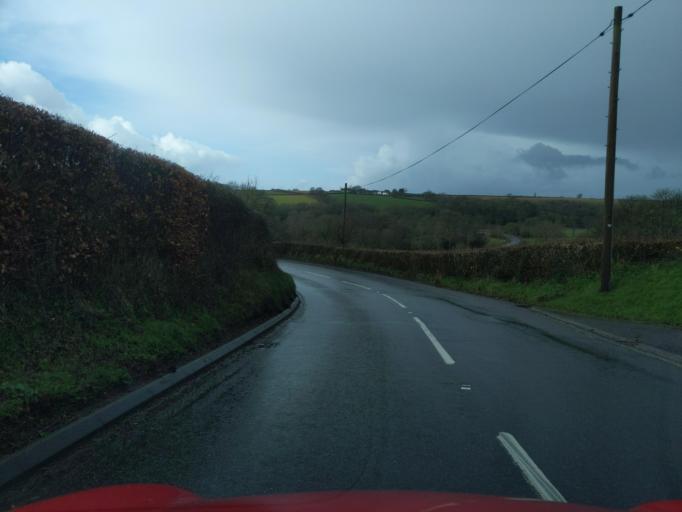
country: GB
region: England
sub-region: Devon
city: Okehampton
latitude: 50.8338
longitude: -4.0751
